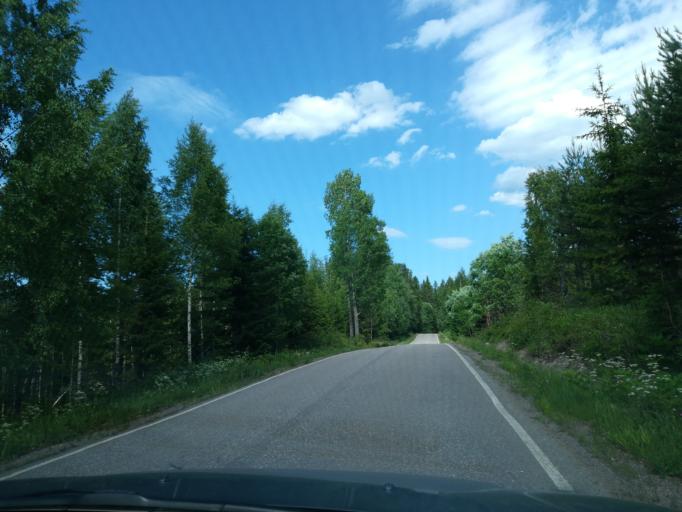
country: FI
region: South Karelia
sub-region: Imatra
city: Ruokolahti
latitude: 61.4871
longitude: 28.8776
